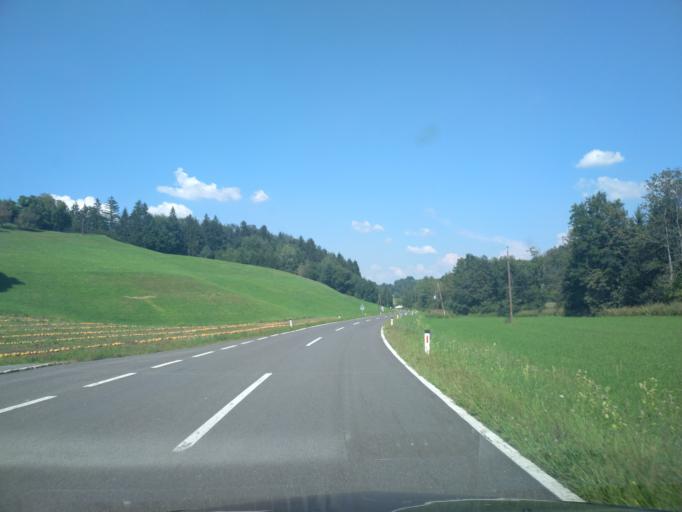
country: AT
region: Styria
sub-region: Politischer Bezirk Leibnitz
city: Sulztal an der Weinstrasse
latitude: 46.7053
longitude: 15.5042
